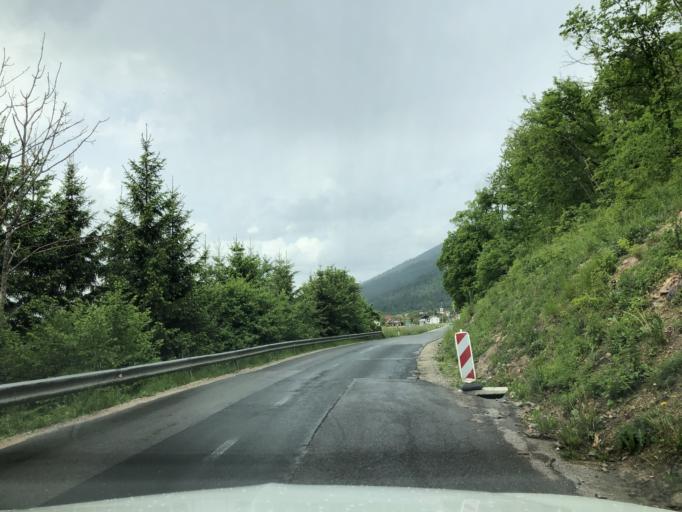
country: SI
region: Cerknica
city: Cerknica
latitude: 45.7642
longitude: 14.4309
